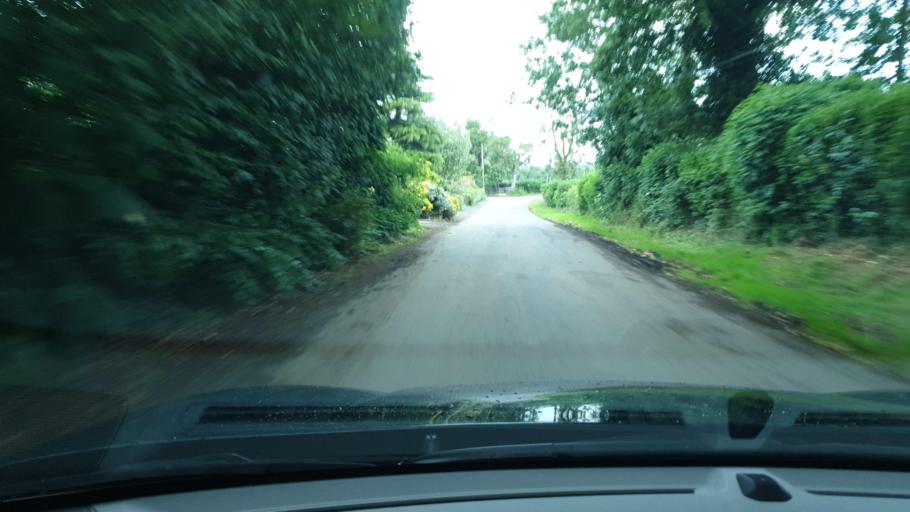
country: IE
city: Kentstown
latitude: 53.5853
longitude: -6.5585
